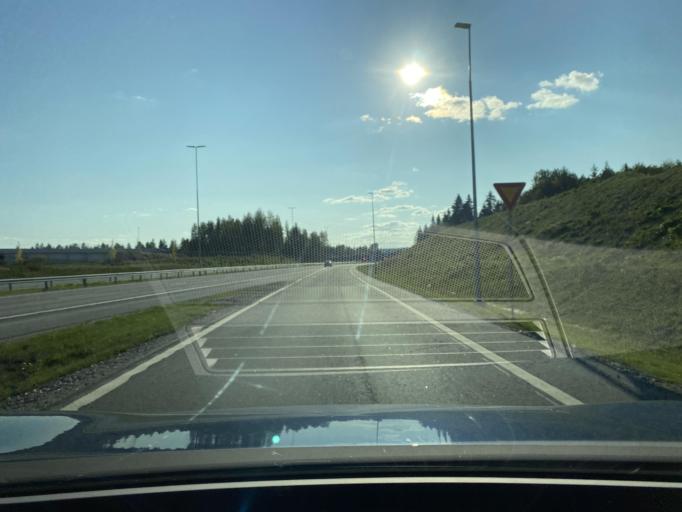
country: FI
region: Paijanne Tavastia
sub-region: Lahti
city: Lahti
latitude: 60.9567
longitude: 25.6491
